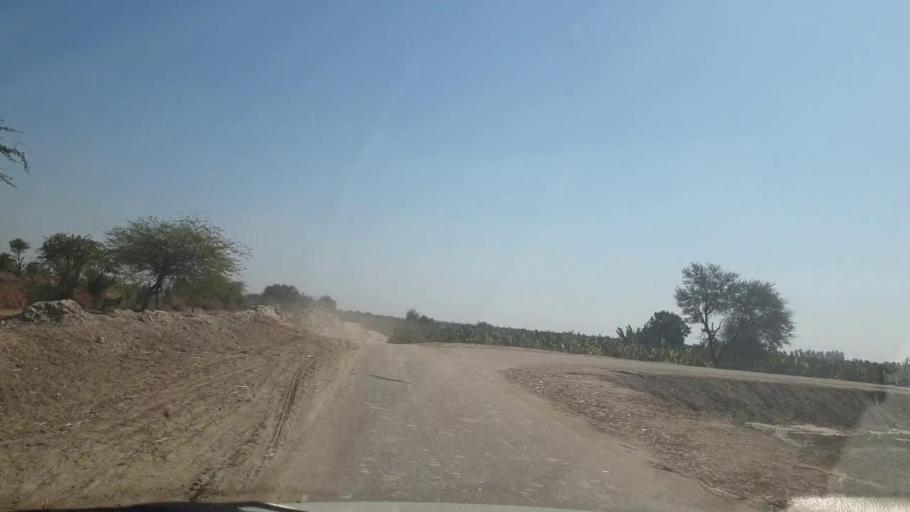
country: PK
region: Sindh
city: Mirpur Khas
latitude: 25.4606
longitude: 69.1812
